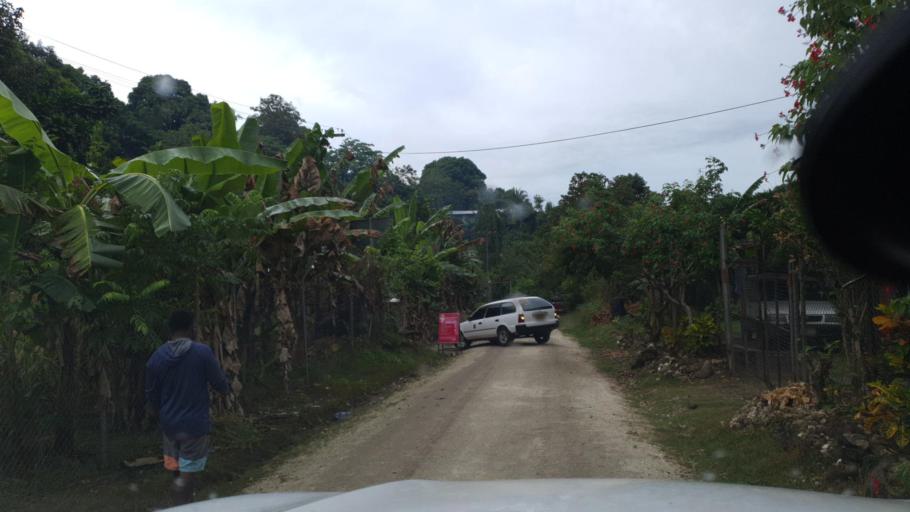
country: SB
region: Guadalcanal
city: Honiara
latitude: -9.4385
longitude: 159.9773
